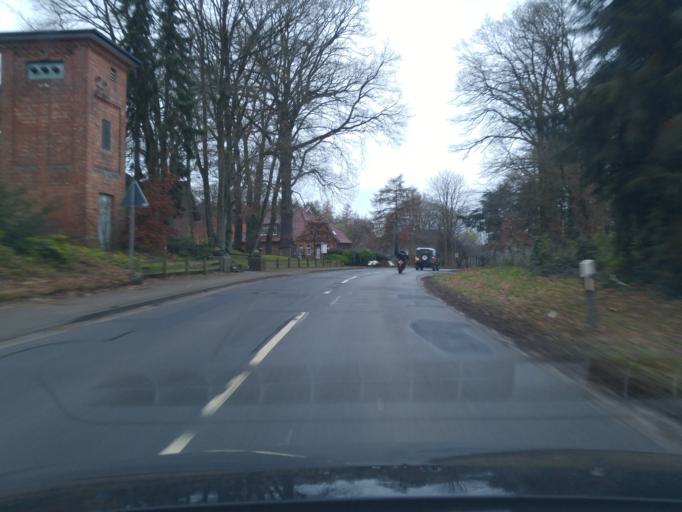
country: DE
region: Lower Saxony
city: Rullstorf
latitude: 53.2676
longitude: 10.5183
